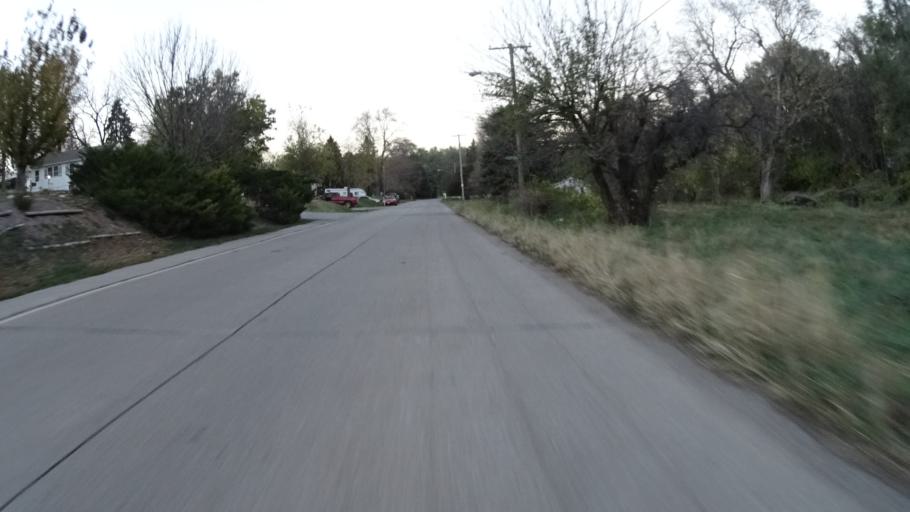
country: US
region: Nebraska
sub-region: Sarpy County
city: Offutt Air Force Base
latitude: 41.1859
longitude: -95.9523
